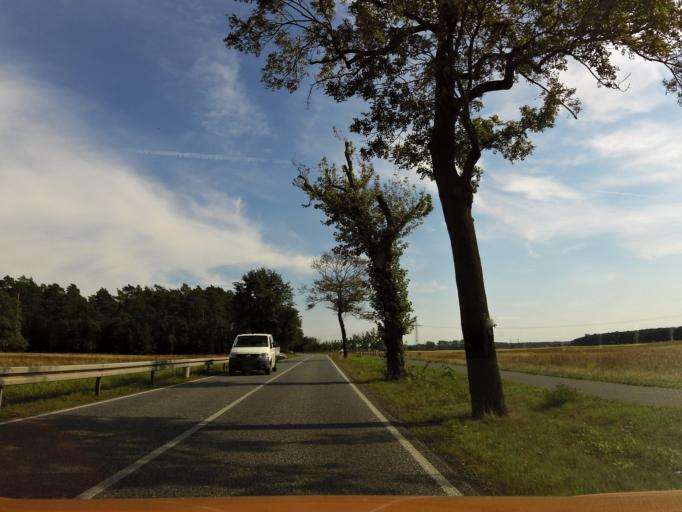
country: DE
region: Brandenburg
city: Stahnsdorf
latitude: 52.3233
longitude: 13.1854
